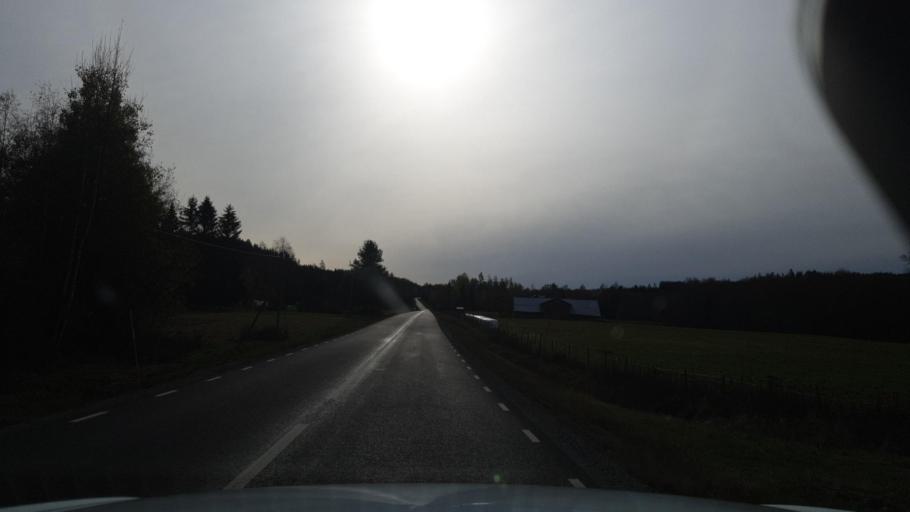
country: SE
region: Vaermland
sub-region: Arjangs Kommun
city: Arjaeng
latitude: 59.5819
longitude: 12.1236
